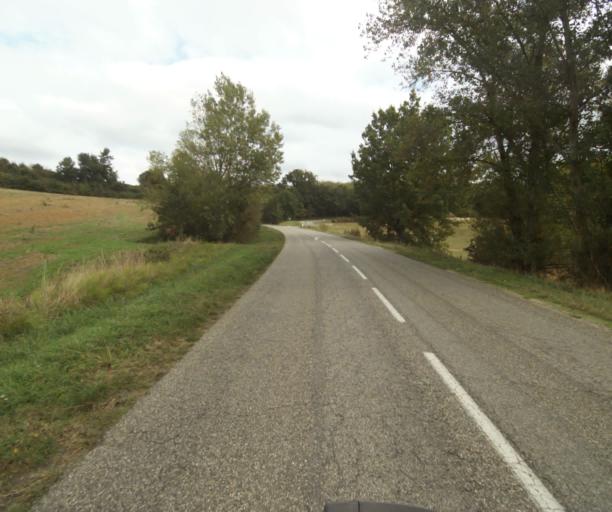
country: FR
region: Midi-Pyrenees
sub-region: Departement du Tarn-et-Garonne
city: Finhan
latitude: 43.8579
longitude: 1.1099
